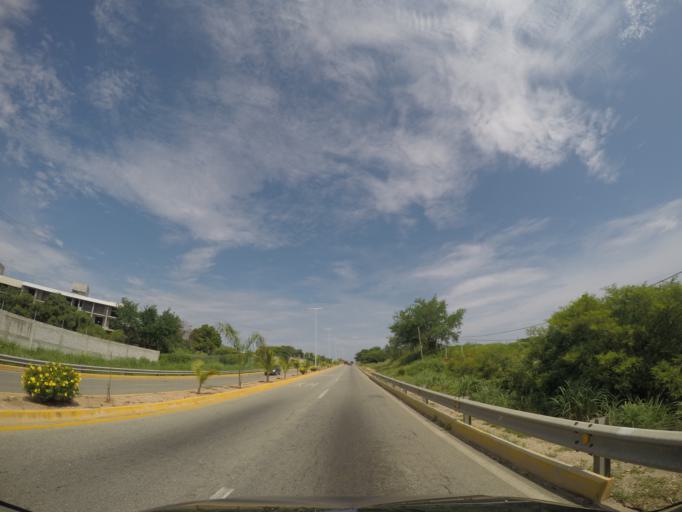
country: MX
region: Oaxaca
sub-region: Santa Maria Colotepec
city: Brisas de Zicatela
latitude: 15.8362
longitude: -97.0382
